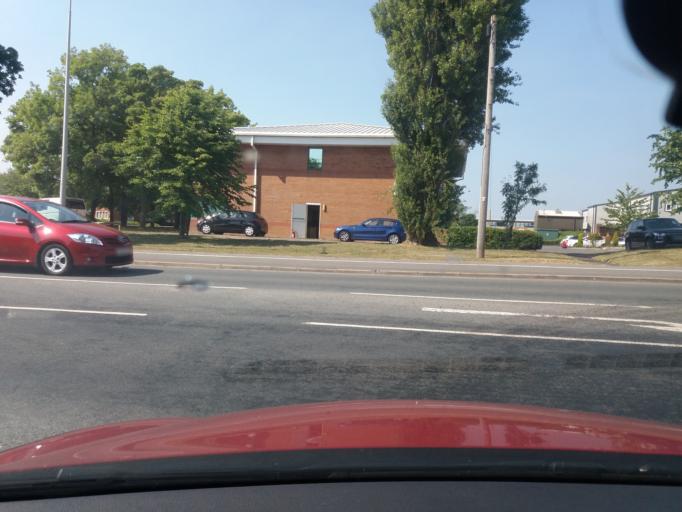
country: GB
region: England
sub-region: Lancashire
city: Euxton
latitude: 53.6719
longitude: -2.6671
